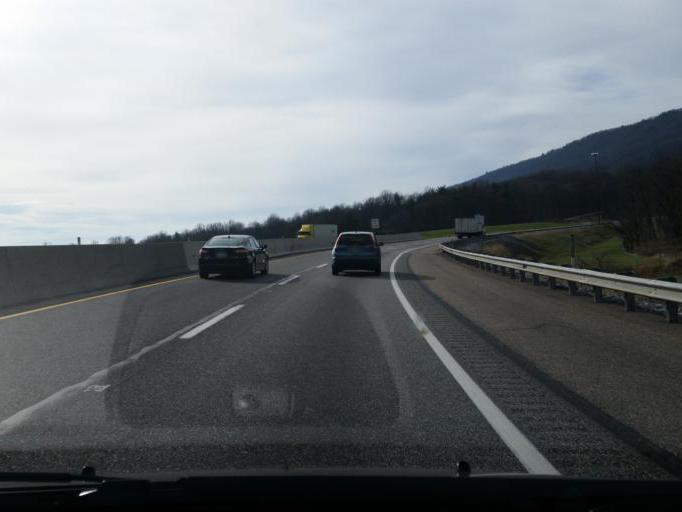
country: US
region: Pennsylvania
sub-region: Franklin County
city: Doylestown
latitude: 40.0883
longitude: -77.8274
